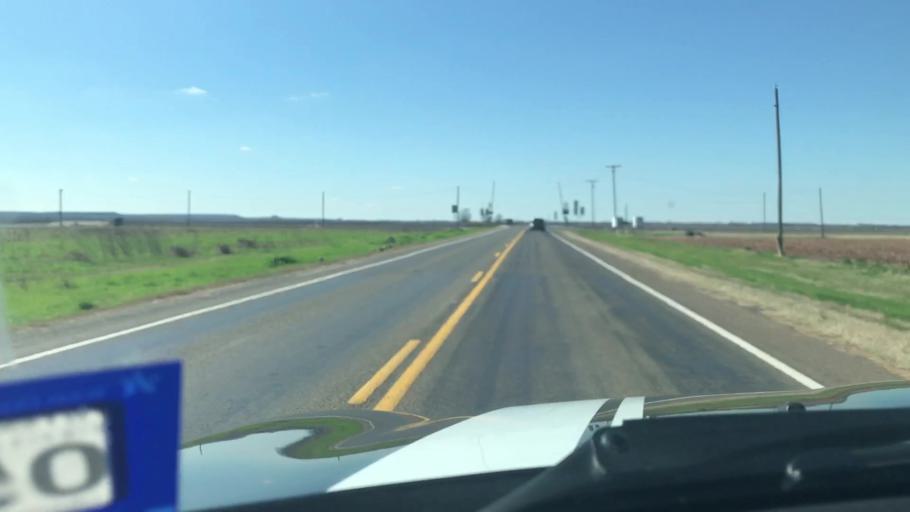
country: US
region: Texas
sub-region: Robertson County
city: Hearne
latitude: 30.8733
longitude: -96.6596
